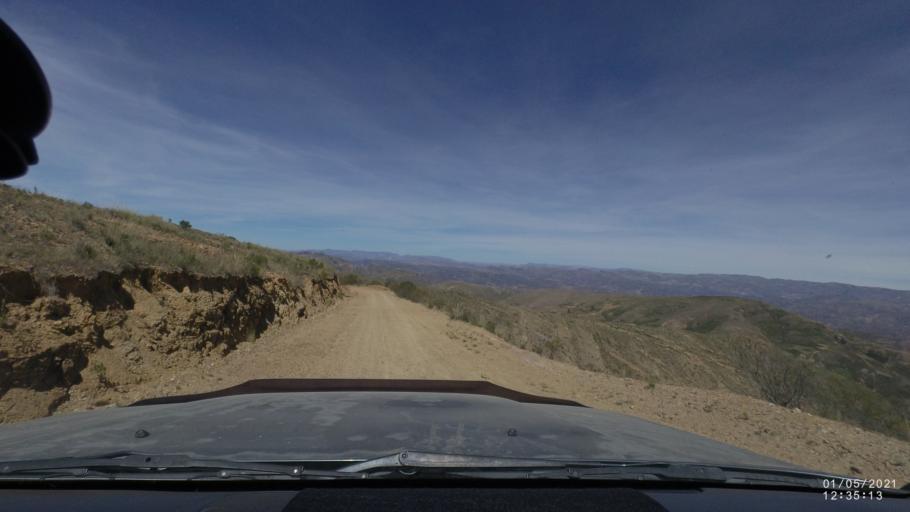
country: BO
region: Cochabamba
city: Capinota
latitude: -17.6776
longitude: -66.1553
